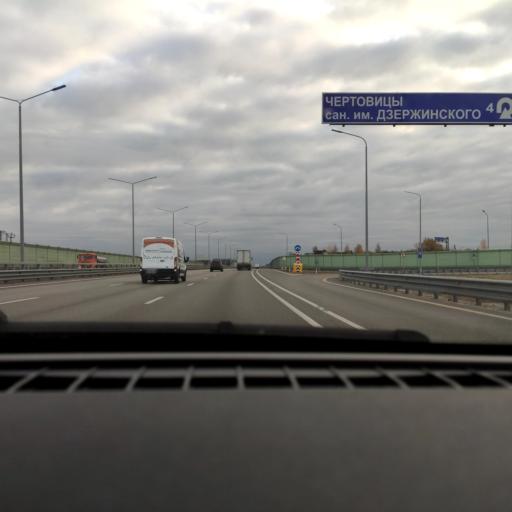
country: RU
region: Voronezj
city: Ramon'
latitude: 51.8217
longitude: 39.2505
